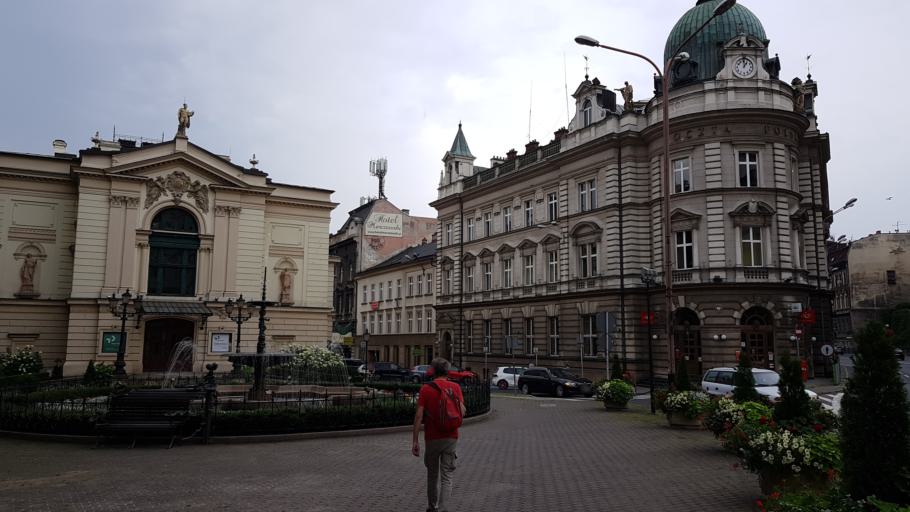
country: PL
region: Silesian Voivodeship
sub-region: Bielsko-Biala
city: Bielsko-Biala
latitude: 49.8214
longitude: 19.0451
